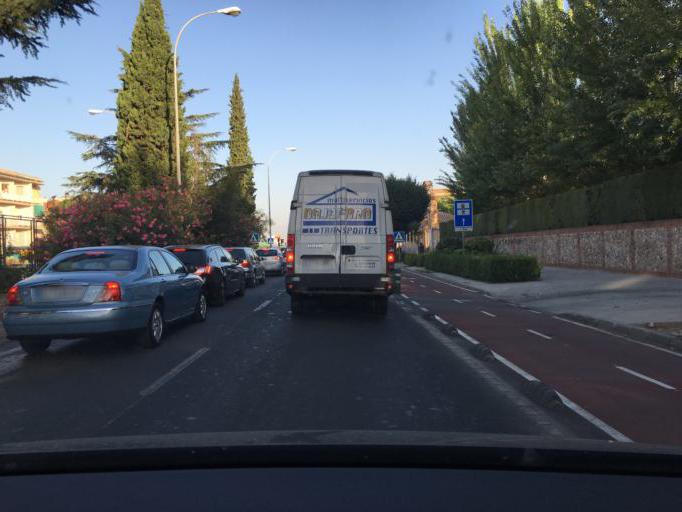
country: ES
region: Andalusia
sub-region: Provincia de Granada
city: Maracena
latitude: 37.1943
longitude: -3.6262
